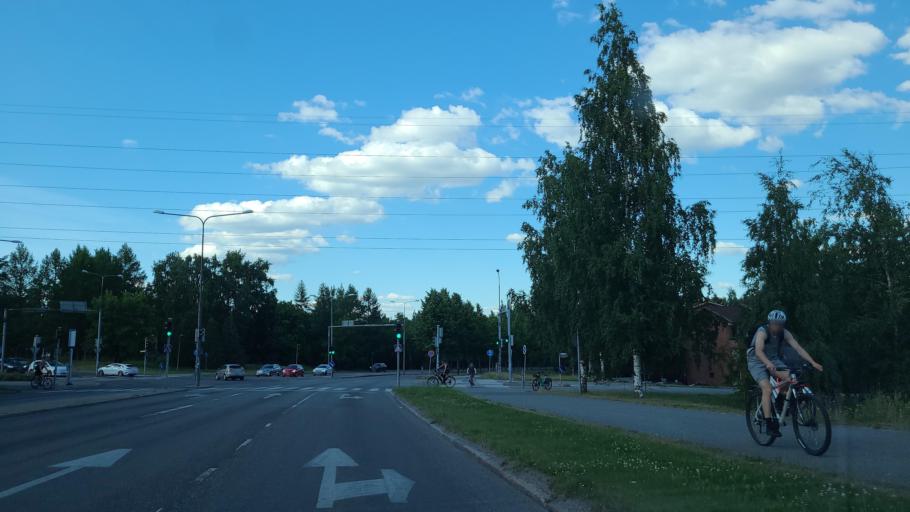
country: FI
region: Central Finland
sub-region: Jyvaeskylae
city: Jyvaeskylae
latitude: 62.2541
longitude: 25.7506
